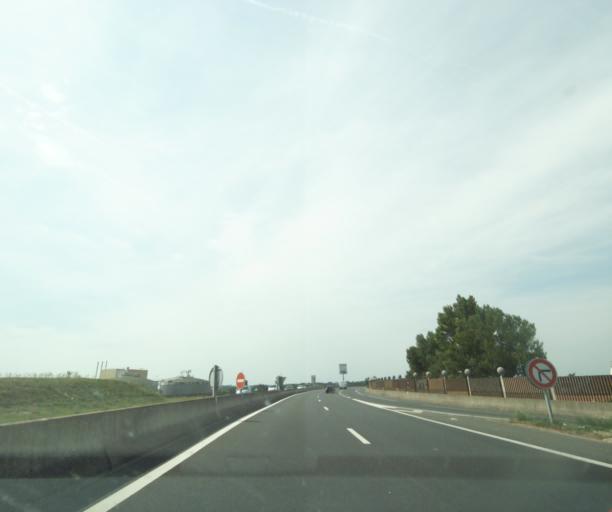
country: FR
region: Centre
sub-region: Departement d'Indre-et-Loire
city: La Riche
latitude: 47.3769
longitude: 0.6507
